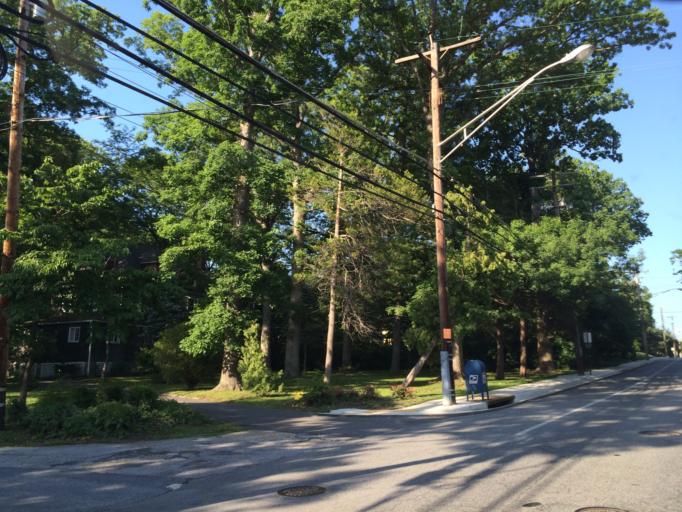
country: US
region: Maryland
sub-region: Baltimore County
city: Catonsville
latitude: 39.2745
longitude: -76.7480
